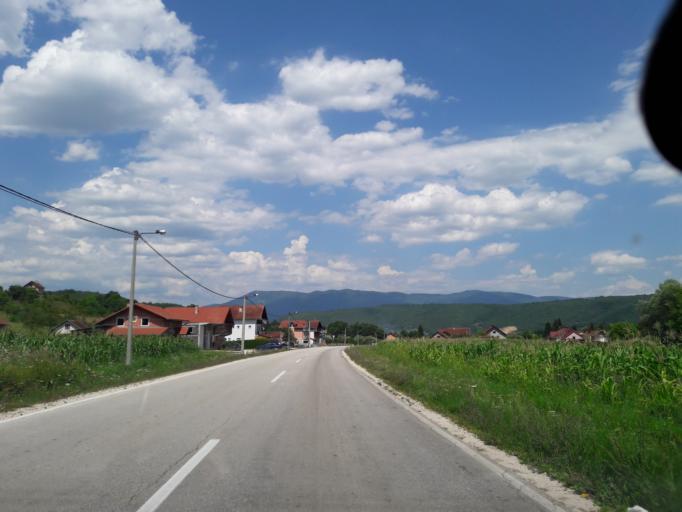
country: BA
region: Republika Srpska
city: Mrkonjic Grad
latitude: 44.4284
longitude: 17.1362
